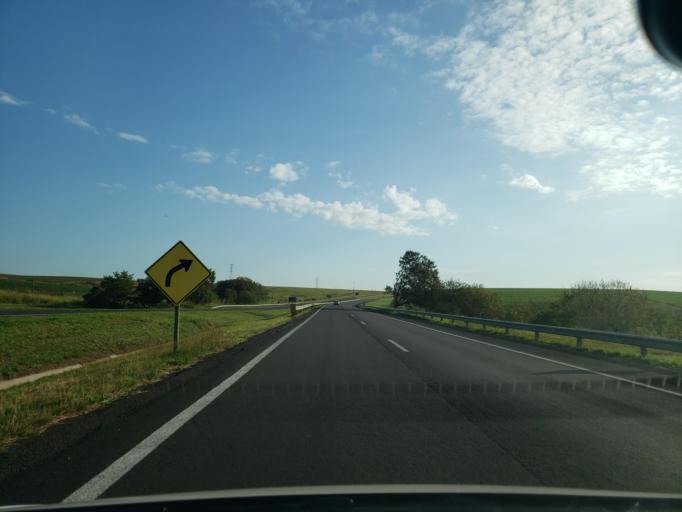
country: BR
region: Sao Paulo
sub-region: Valparaiso
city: Valparaiso
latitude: -21.2158
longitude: -50.8409
